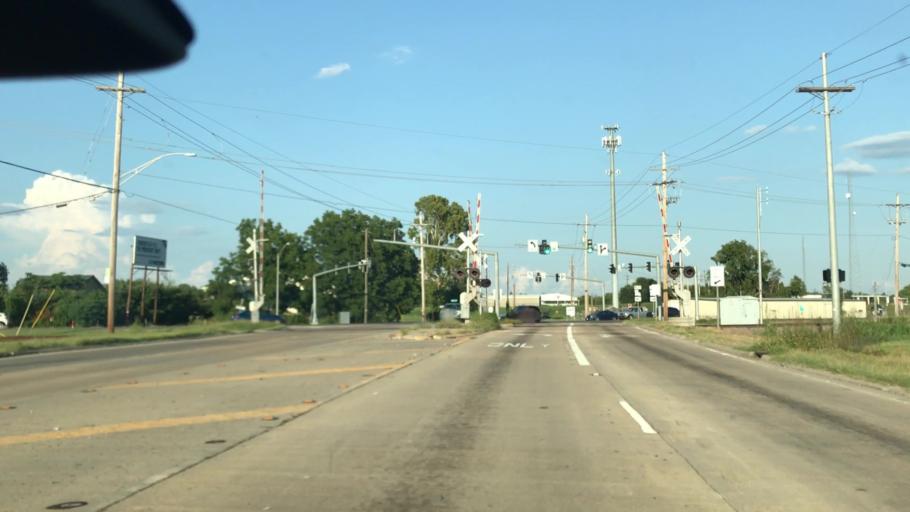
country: US
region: Louisiana
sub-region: Bossier Parish
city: Bossier City
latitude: 32.4008
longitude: -93.6944
